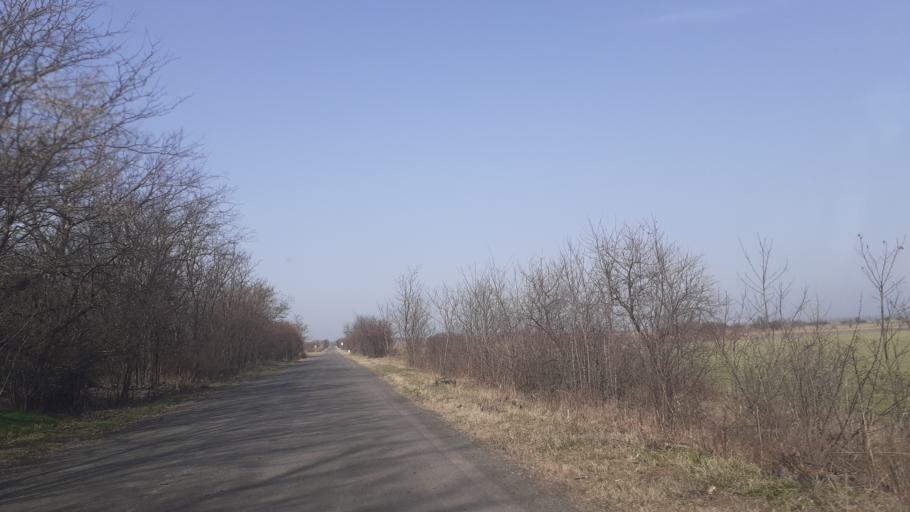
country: HU
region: Pest
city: Dabas
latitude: 47.1247
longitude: 19.2101
